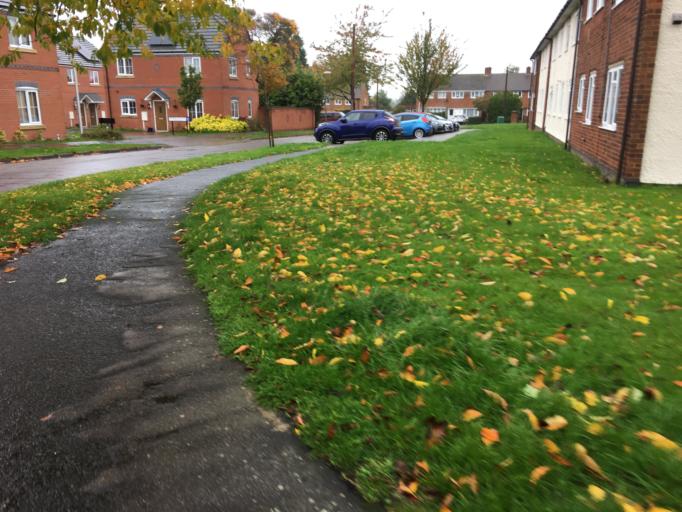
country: GB
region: England
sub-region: Warwickshire
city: Rugby
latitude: 52.3620
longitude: -1.2246
